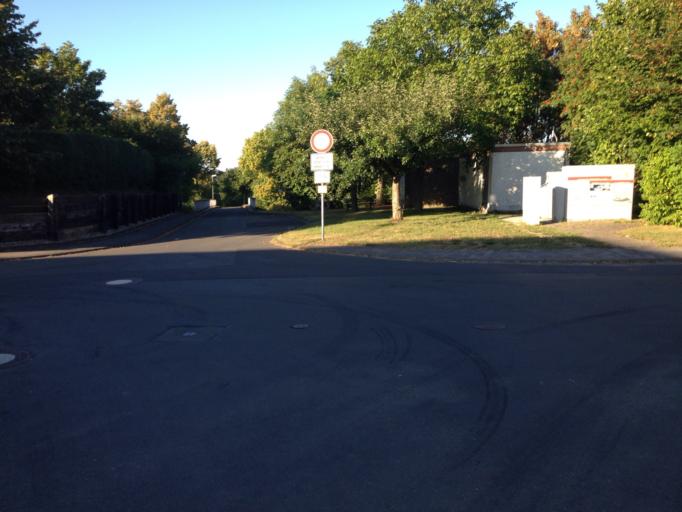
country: DE
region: Hesse
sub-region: Regierungsbezirk Giessen
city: Lich
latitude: 50.5467
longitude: 8.7750
